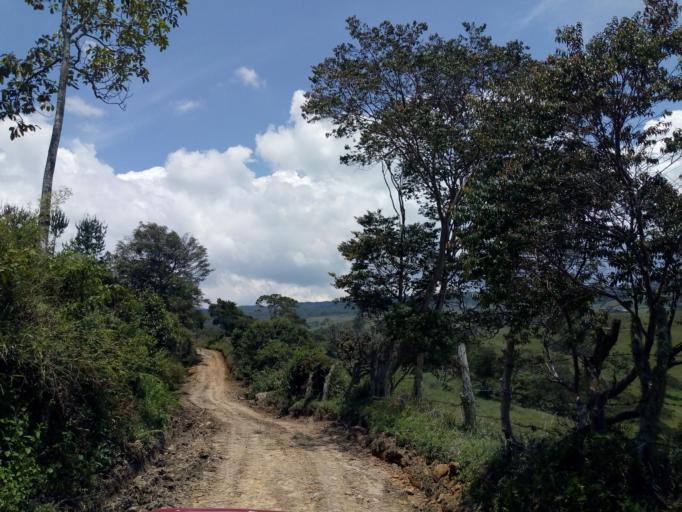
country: CO
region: Boyaca
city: Moniquira
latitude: 5.8697
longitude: -73.5054
